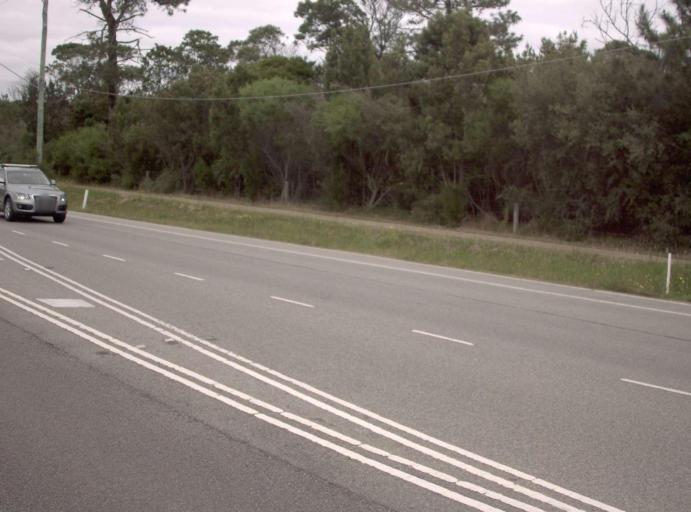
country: AU
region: Victoria
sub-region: Mornington Peninsula
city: Mount Martha
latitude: -38.2566
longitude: 145.0357
